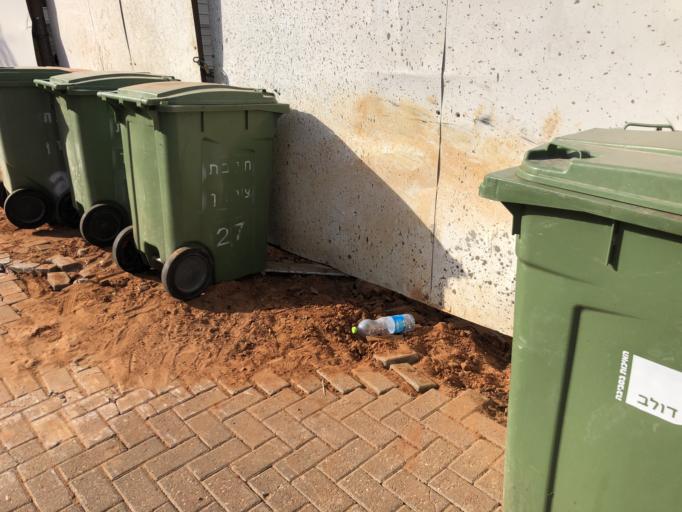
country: IL
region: Tel Aviv
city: Bene Beraq
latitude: 32.0794
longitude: 34.8232
